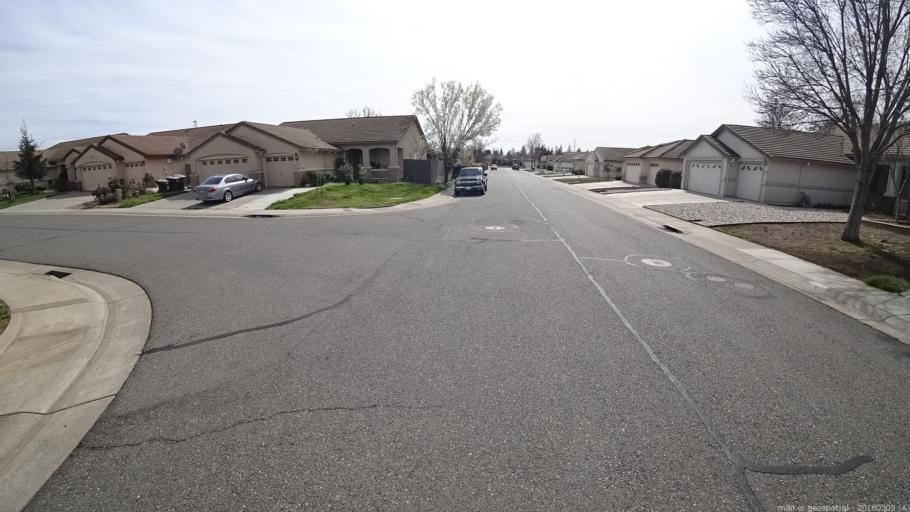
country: US
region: California
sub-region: Sacramento County
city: Vineyard
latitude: 38.4547
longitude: -121.3552
